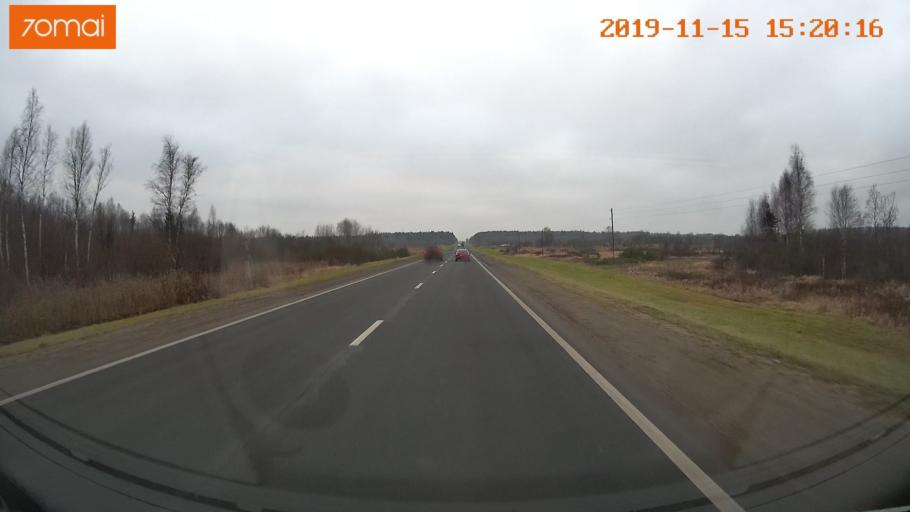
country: RU
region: Jaroslavl
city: Danilov
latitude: 58.2255
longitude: 40.1646
